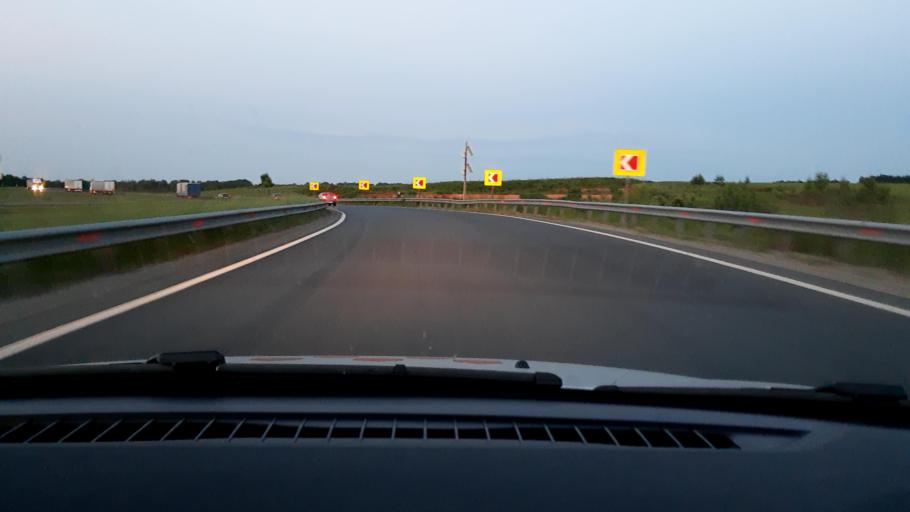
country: RU
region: Nizjnij Novgorod
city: Kstovo
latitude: 56.0664
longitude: 44.1208
